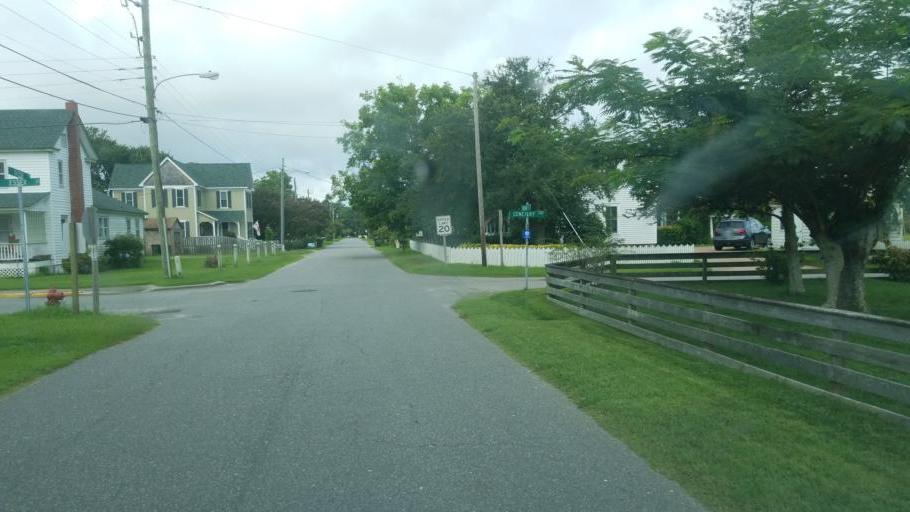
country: US
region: North Carolina
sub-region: Dare County
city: Manteo
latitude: 35.9108
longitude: -75.6722
